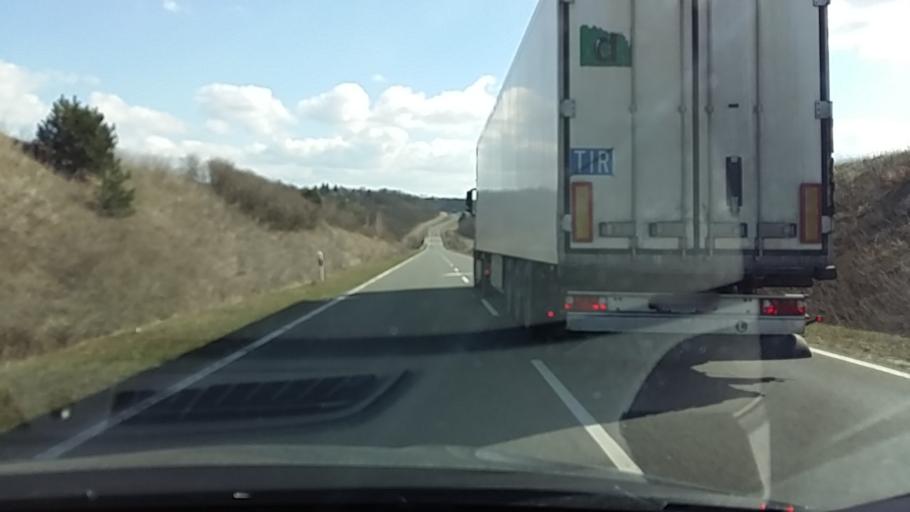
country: HU
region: Baranya
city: Kozarmisleny
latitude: 46.0302
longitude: 18.2756
